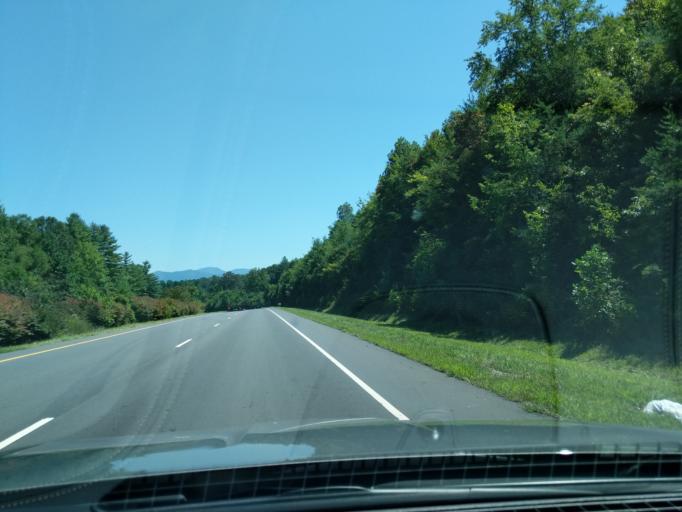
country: US
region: North Carolina
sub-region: Macon County
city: Franklin
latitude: 35.1642
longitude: -83.4199
